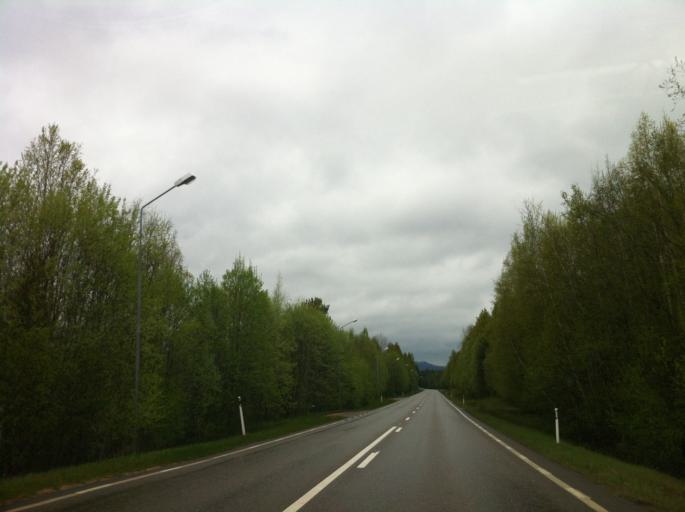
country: SE
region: Jaemtland
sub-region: Harjedalens Kommun
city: Sveg
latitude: 62.0661
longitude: 14.2732
